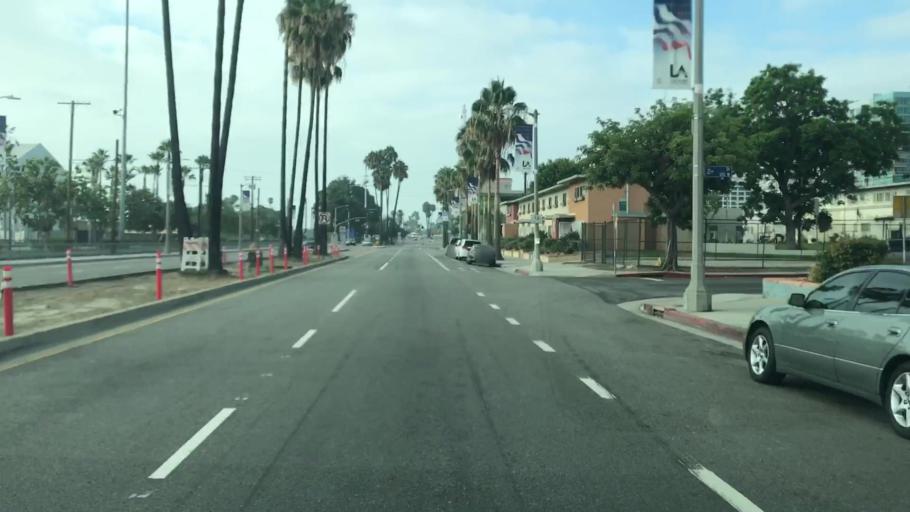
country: US
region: California
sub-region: Los Angeles County
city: San Pedro
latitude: 33.7430
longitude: -118.2798
